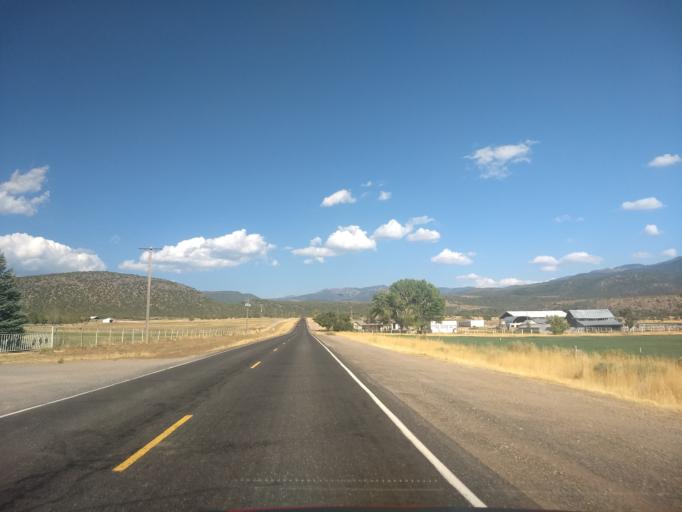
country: US
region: Utah
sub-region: Washington County
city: Enterprise
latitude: 37.4170
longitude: -113.6196
